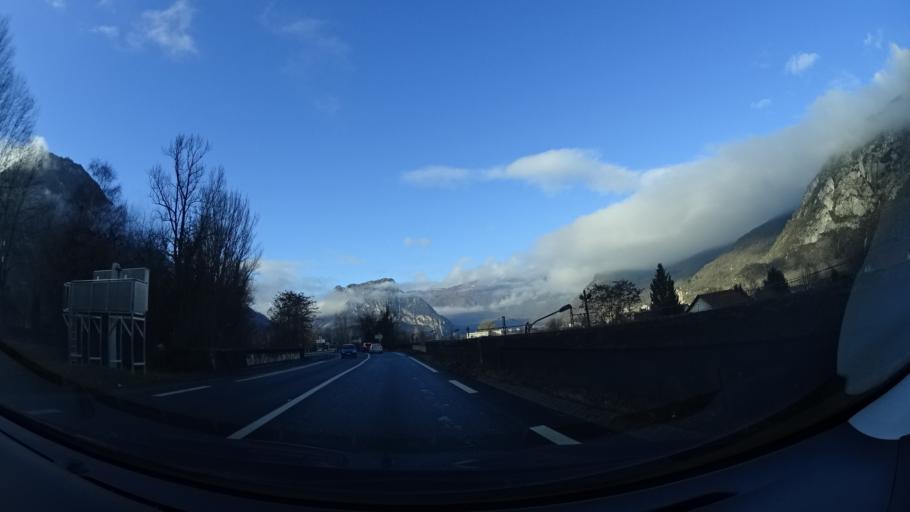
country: FR
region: Midi-Pyrenees
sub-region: Departement de l'Ariege
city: Tarascon-sur-Ariege
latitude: 42.8364
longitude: 1.6061
